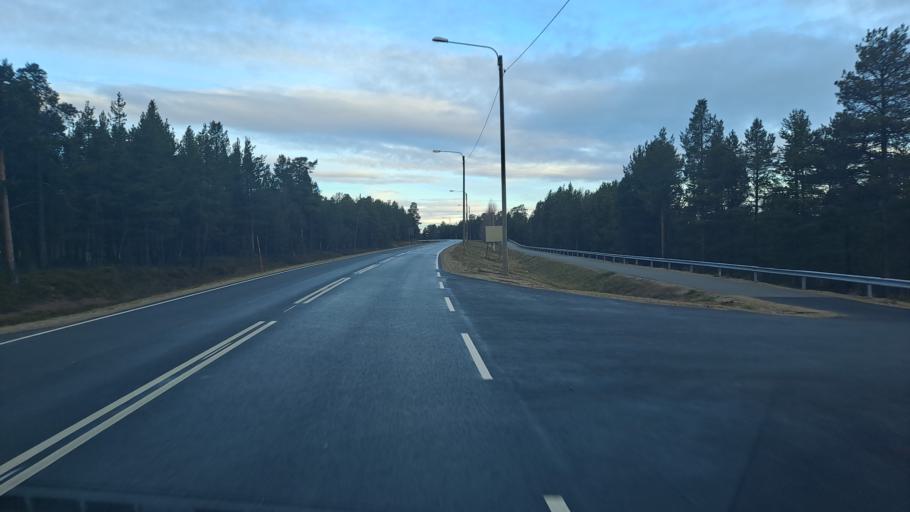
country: FI
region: Lapland
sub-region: Pohjois-Lappi
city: Inari
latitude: 68.8986
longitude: 27.0817
